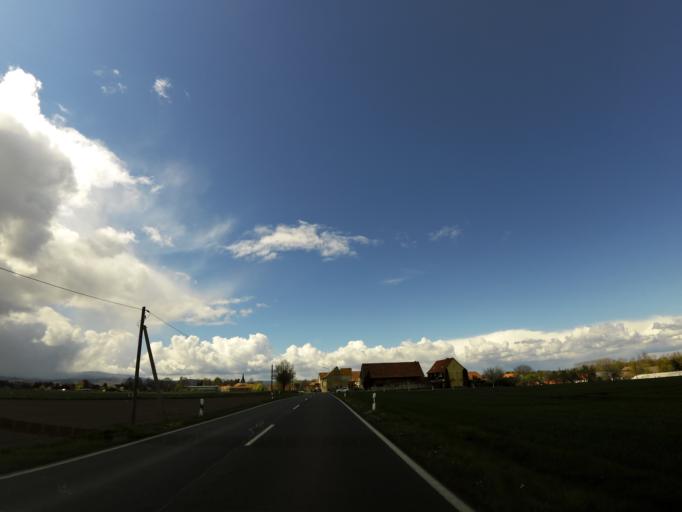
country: DE
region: Saxony-Anhalt
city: Heudeber
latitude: 51.8618
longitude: 10.8569
